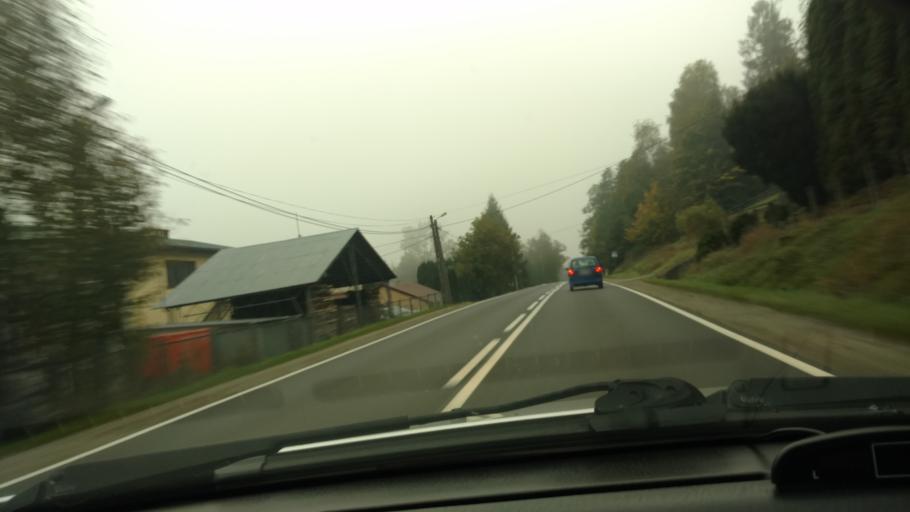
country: PL
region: Subcarpathian Voivodeship
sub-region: Powiat strzyzowski
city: Frysztak
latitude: 49.8356
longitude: 21.6123
